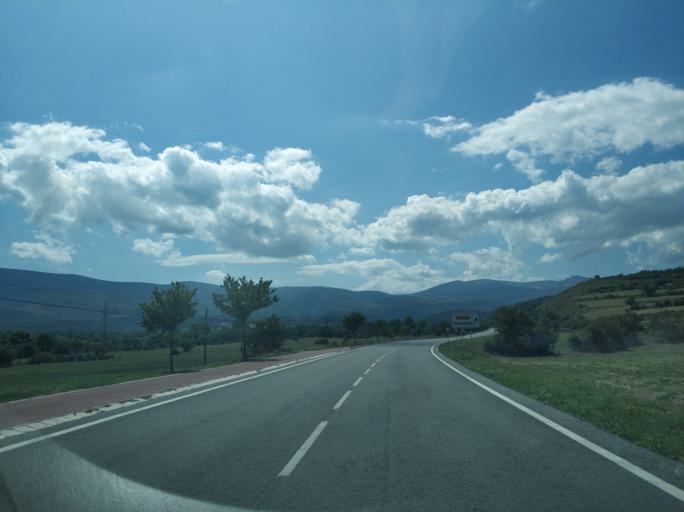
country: ES
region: Cantabria
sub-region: Provincia de Cantabria
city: Villaescusa
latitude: 43.0210
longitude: -4.2359
